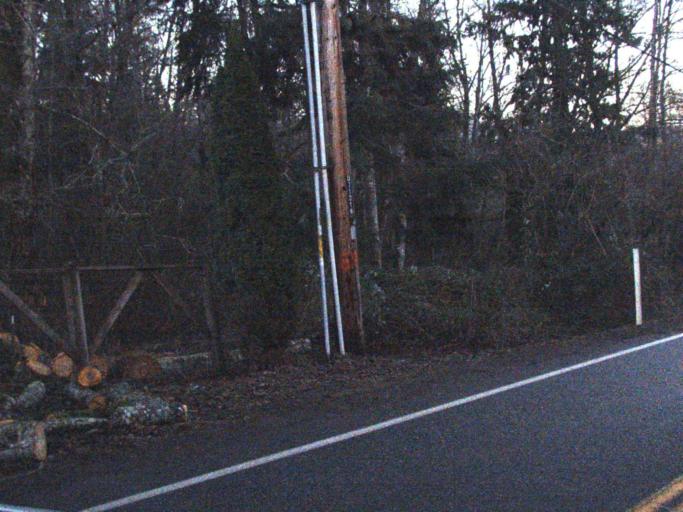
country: US
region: Washington
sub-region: Skagit County
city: Big Lake
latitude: 48.3207
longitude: -122.2449
